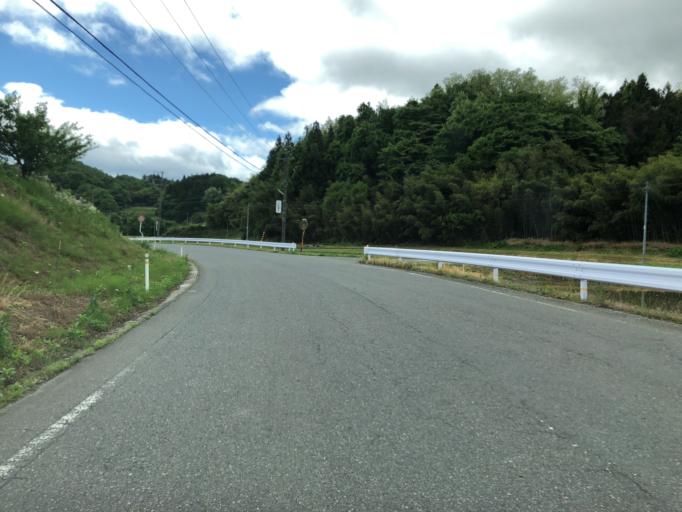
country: JP
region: Fukushima
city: Miharu
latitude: 37.4645
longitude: 140.4750
